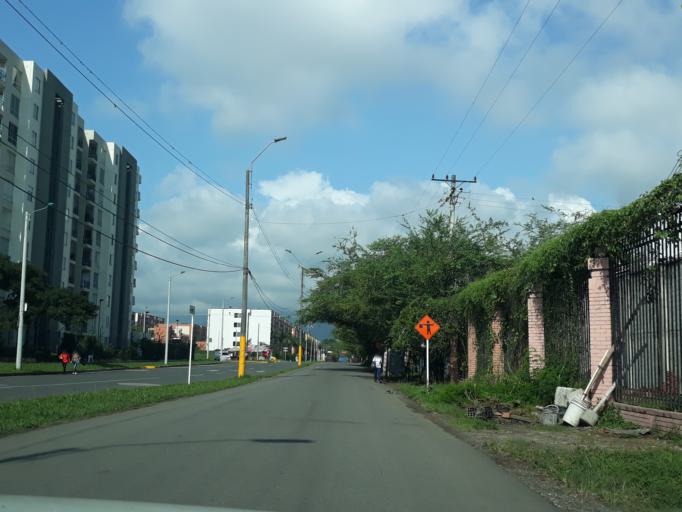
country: CO
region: Valle del Cauca
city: Cali
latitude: 3.3585
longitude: -76.5146
